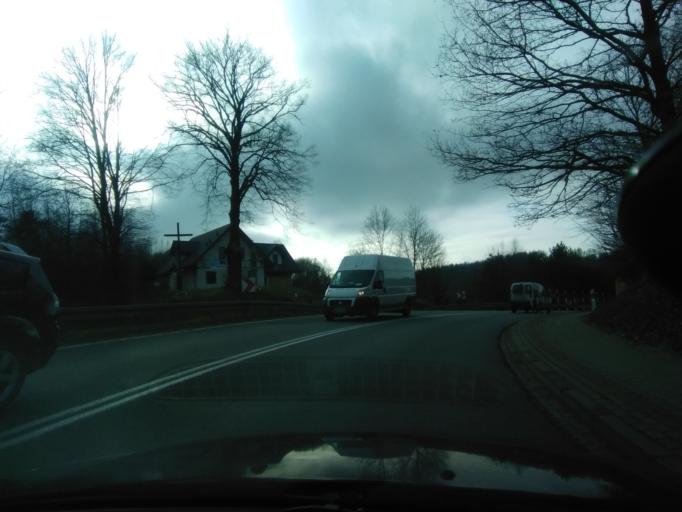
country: PL
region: Subcarpathian Voivodeship
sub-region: Powiat brzozowski
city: Domaradz
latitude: 49.7702
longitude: 21.9434
